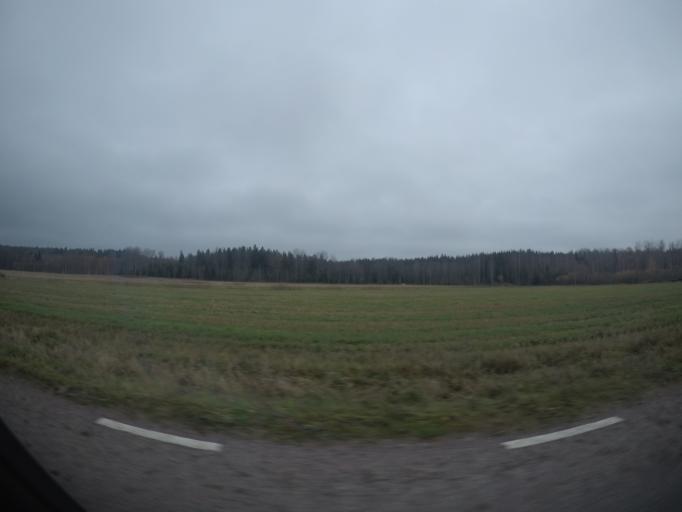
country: SE
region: Vaestmanland
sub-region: Surahammars Kommun
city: Surahammar
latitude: 59.6784
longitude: 16.0815
